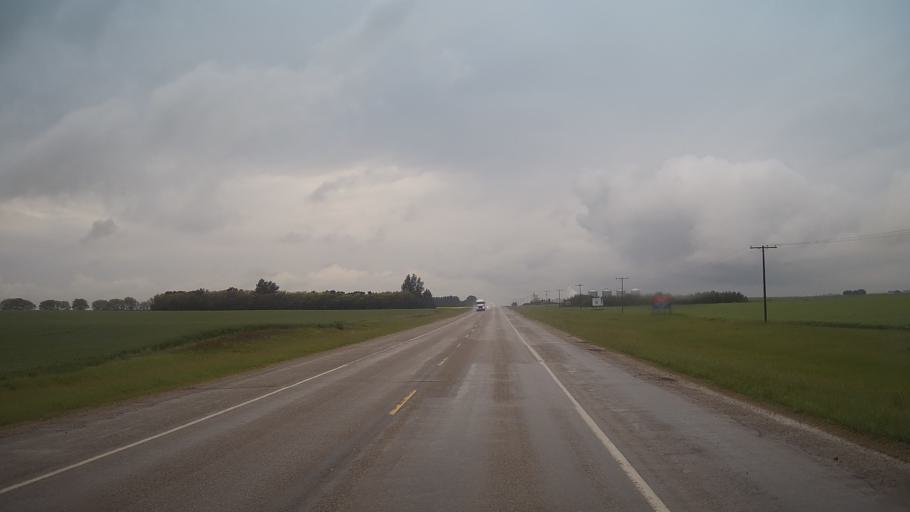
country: CA
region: Saskatchewan
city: Unity
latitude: 52.4350
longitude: -109.0791
